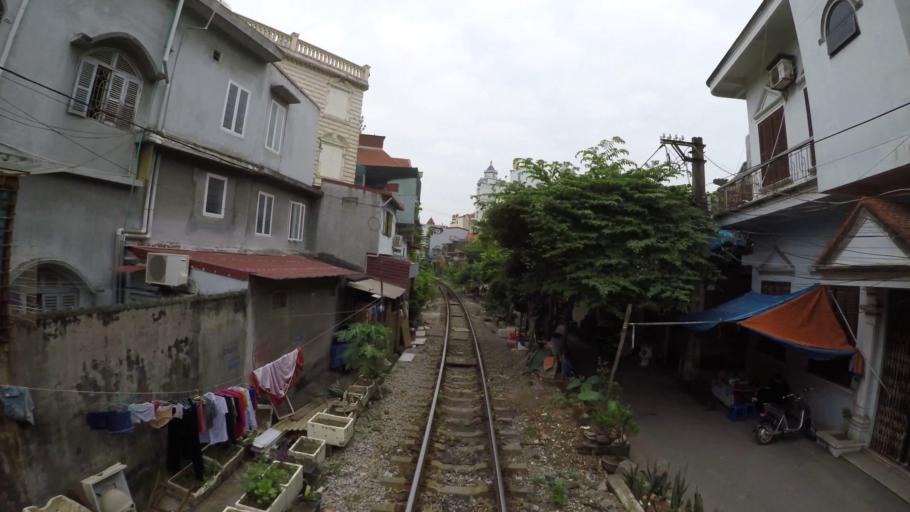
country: VN
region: Hai Phong
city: Haiphong
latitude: 20.8517
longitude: 106.6684
